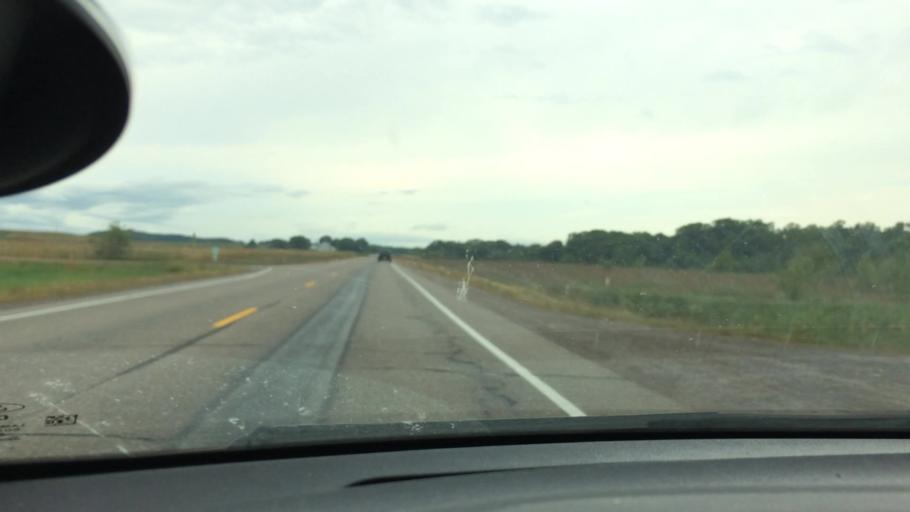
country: US
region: Wisconsin
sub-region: Eau Claire County
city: Augusta
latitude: 44.5855
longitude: -91.1285
